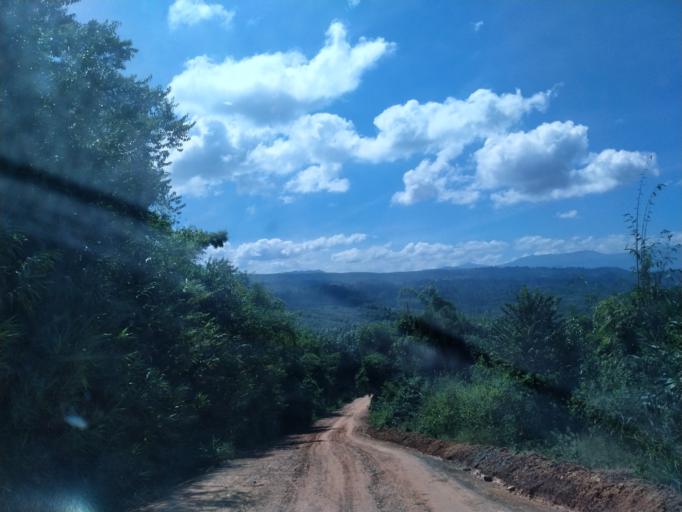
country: LA
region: Vientiane
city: Muang Phon-Hong
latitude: 18.6239
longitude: 102.8748
